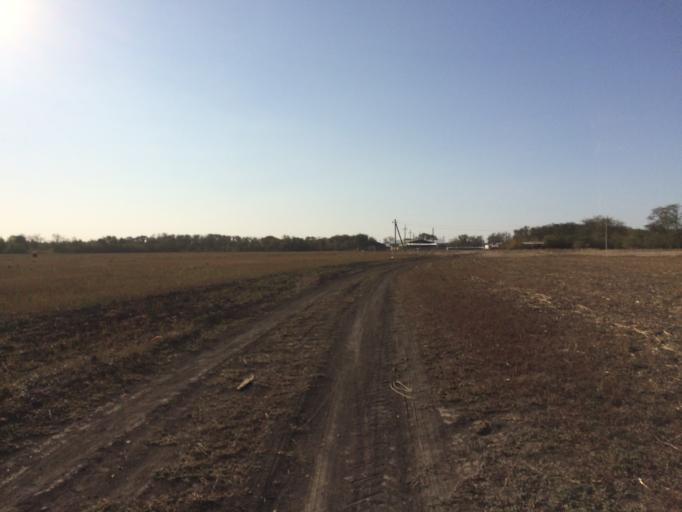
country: RU
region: Rostov
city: Gigant
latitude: 46.5125
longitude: 41.1880
